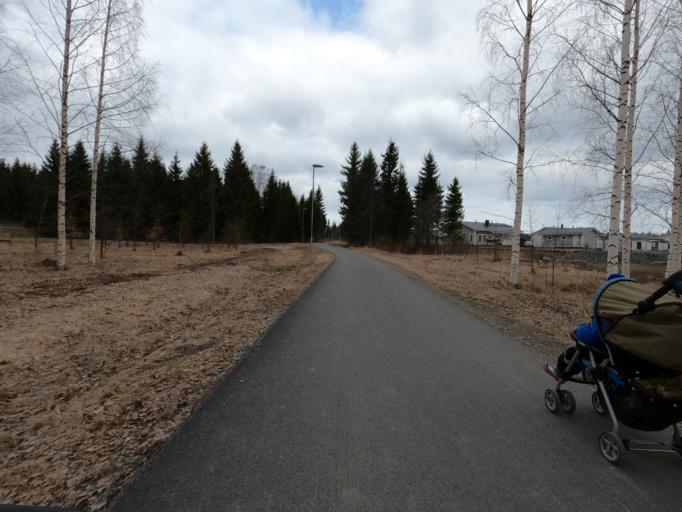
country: FI
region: North Karelia
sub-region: Joensuu
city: Joensuu
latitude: 62.5620
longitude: 29.8220
